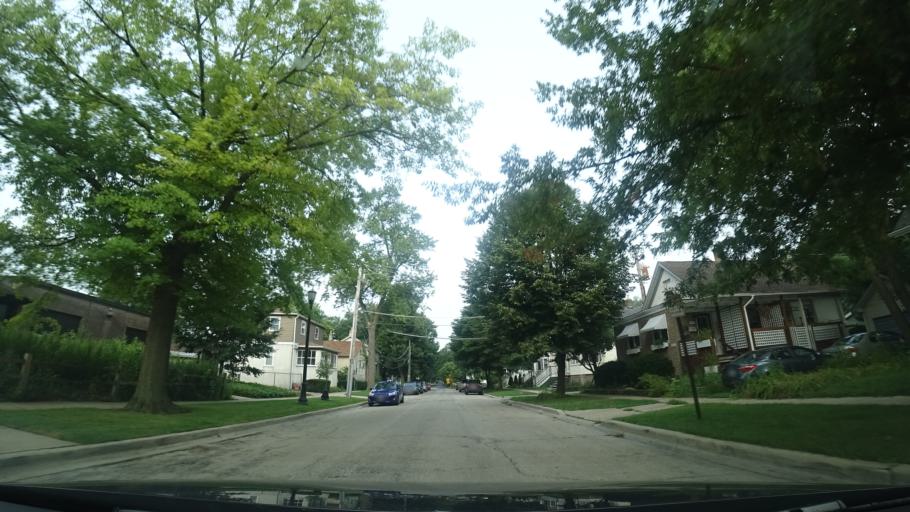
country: US
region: Illinois
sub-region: Cook County
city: Evanston
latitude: 42.0358
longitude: -87.6934
